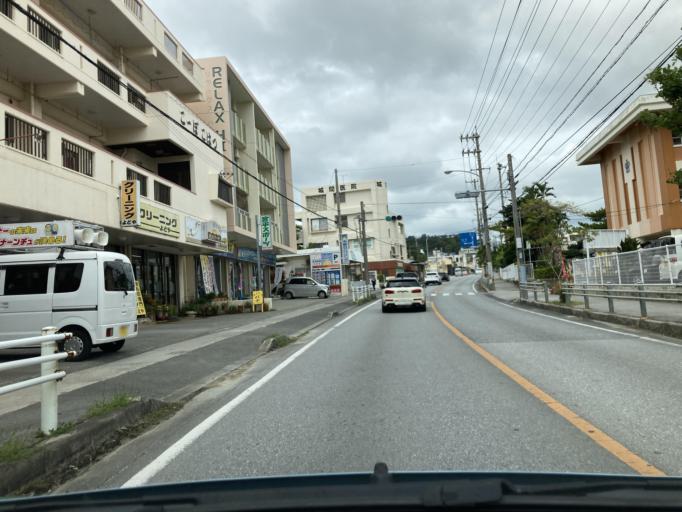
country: JP
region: Okinawa
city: Ginowan
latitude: 26.2282
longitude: 127.7544
